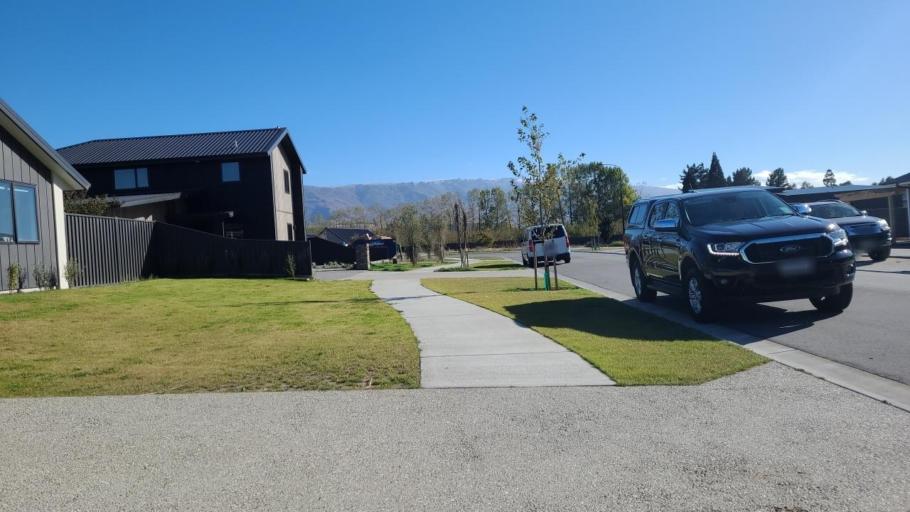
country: NZ
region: Otago
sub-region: Queenstown-Lakes District
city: Wanaka
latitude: -45.0384
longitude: 169.2123
